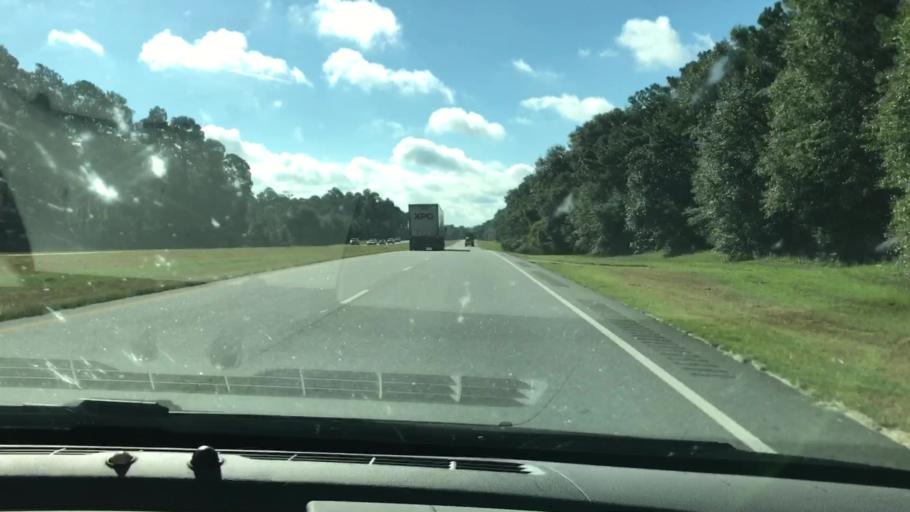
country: US
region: Georgia
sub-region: Dougherty County
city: Putney
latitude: 31.5622
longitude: -84.0127
